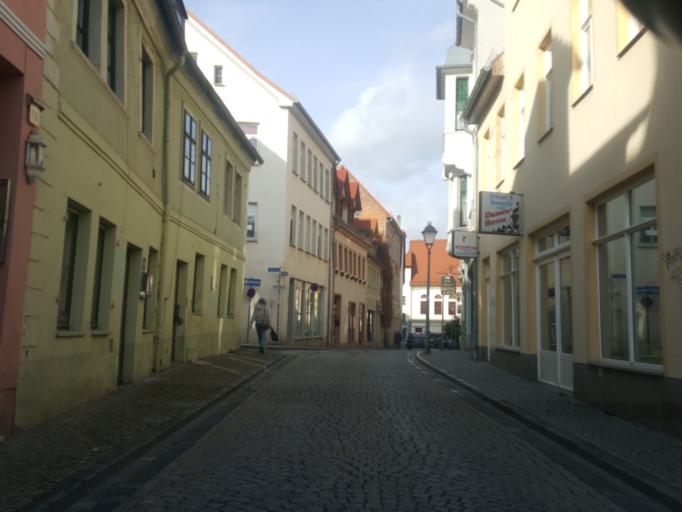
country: DE
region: Saxony-Anhalt
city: Wimmelburg
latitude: 51.5274
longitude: 11.5475
